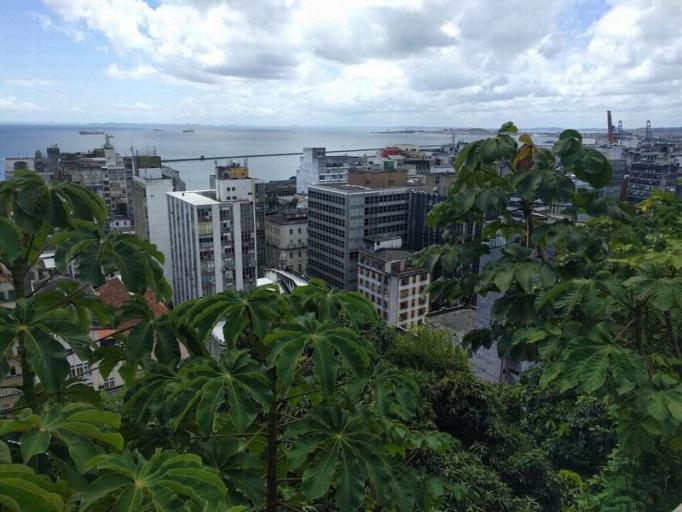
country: BR
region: Bahia
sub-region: Salvador
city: Salvador
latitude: -12.9733
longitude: -38.5120
